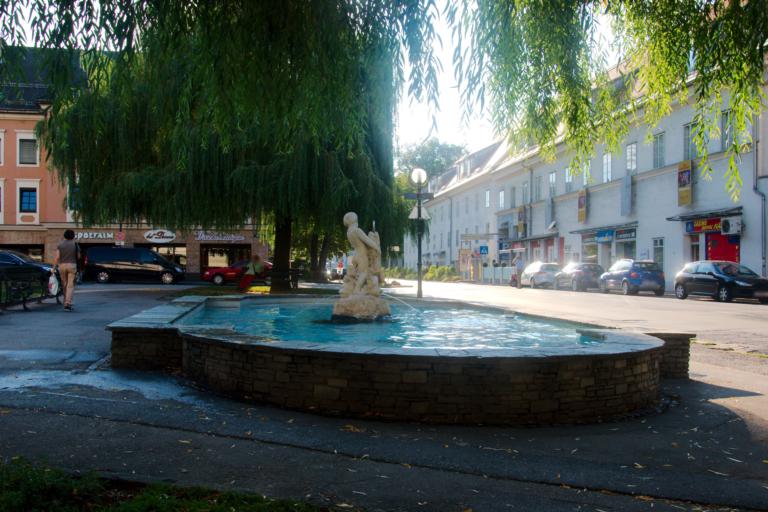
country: AT
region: Carinthia
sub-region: Klagenfurt am Woerthersee
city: Klagenfurt am Woerthersee
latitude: 46.6264
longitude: 14.3076
